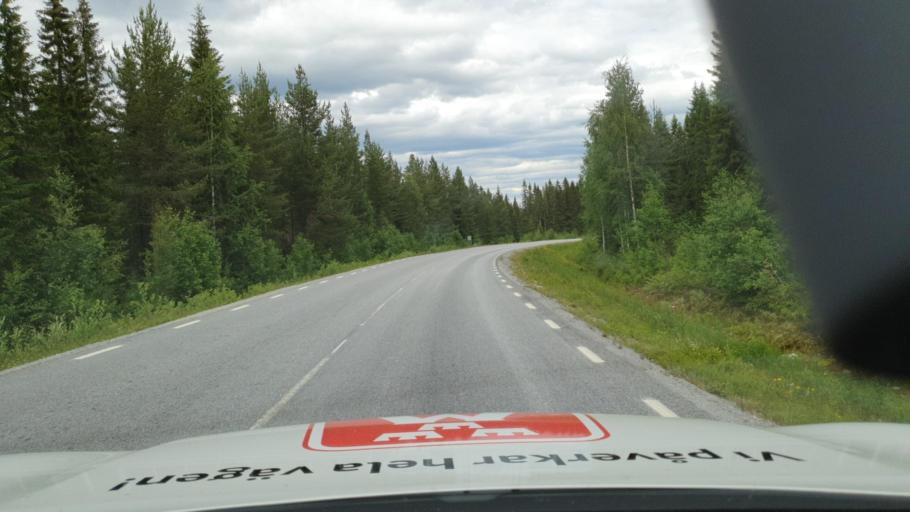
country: SE
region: Vaesterbotten
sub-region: Bjurholms Kommun
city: Bjurholm
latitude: 63.9014
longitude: 19.0773
